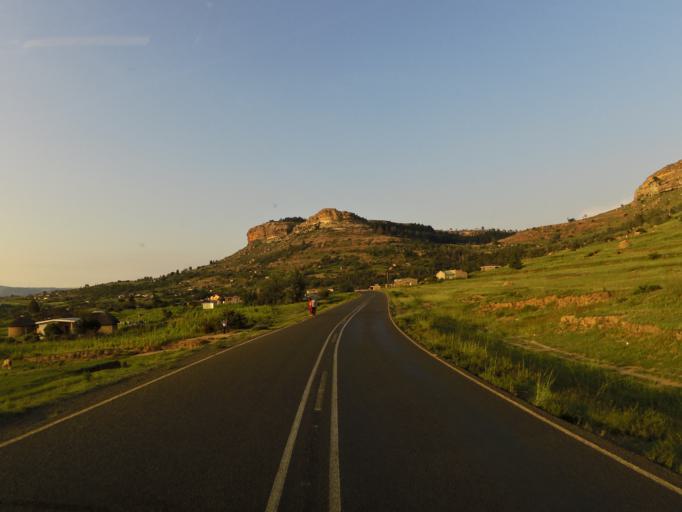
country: LS
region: Leribe
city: Leribe
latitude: -28.9609
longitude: 28.1716
